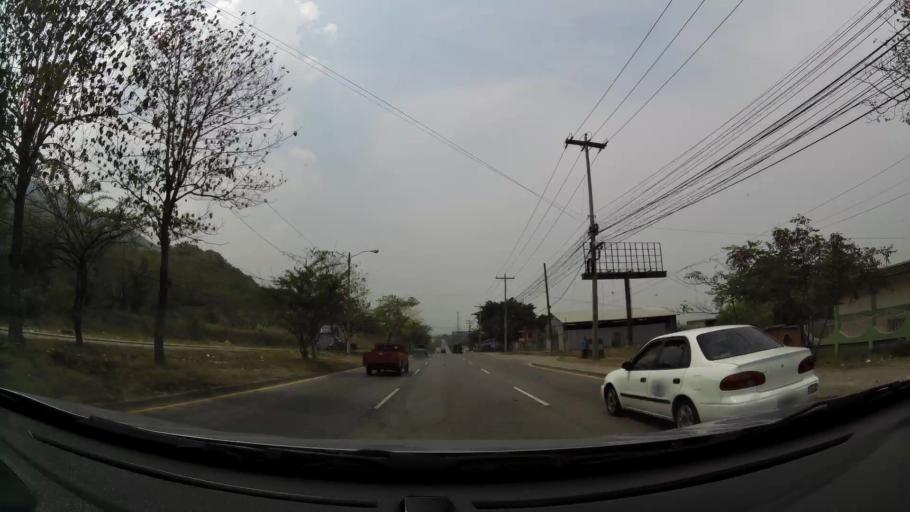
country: HN
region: Cortes
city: Chotepe
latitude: 15.4446
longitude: -88.0212
